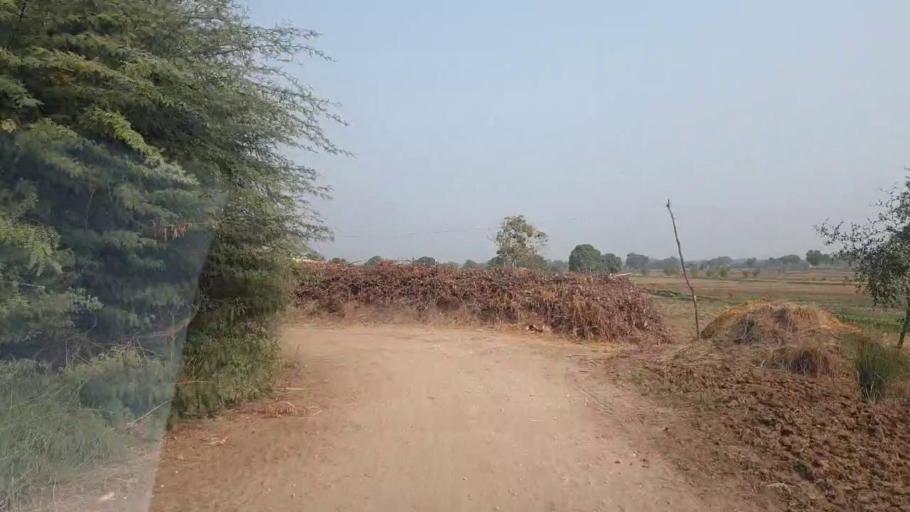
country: PK
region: Sindh
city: Tando Jam
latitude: 25.3305
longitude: 68.5207
